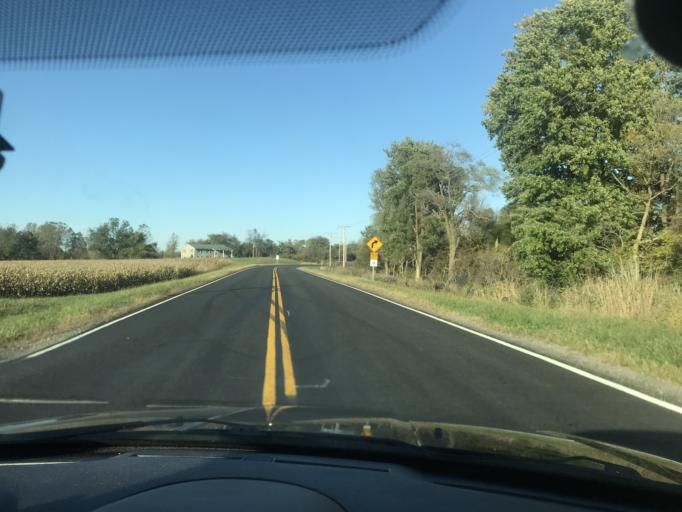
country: US
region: Ohio
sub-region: Logan County
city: Bellefontaine
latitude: 40.3196
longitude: -83.7941
